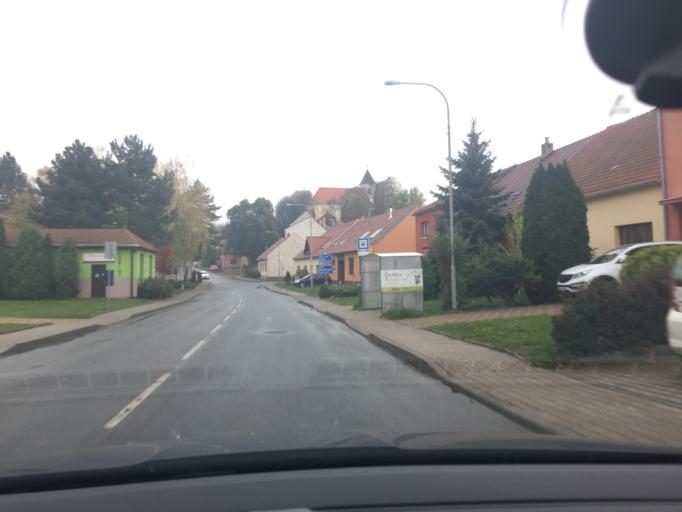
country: CZ
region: South Moravian
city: Blazovice
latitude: 49.1397
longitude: 16.7651
